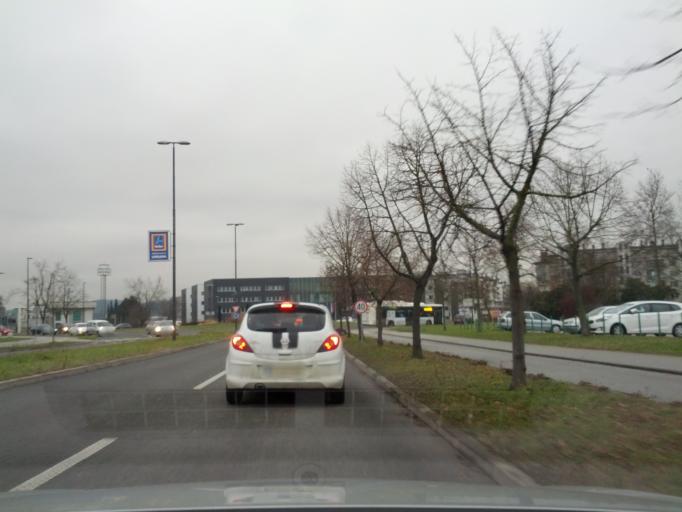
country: SI
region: Ljubljana
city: Ljubljana
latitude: 46.0676
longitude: 14.5263
